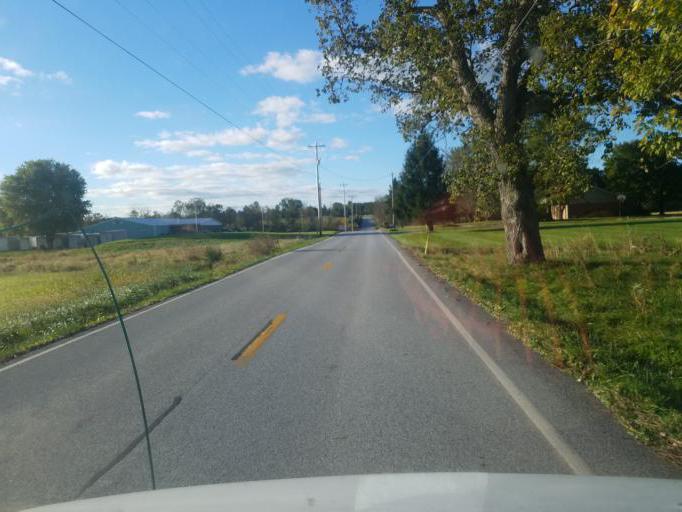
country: US
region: Pennsylvania
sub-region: Adams County
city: Gettysburg
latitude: 39.8782
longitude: -77.2302
